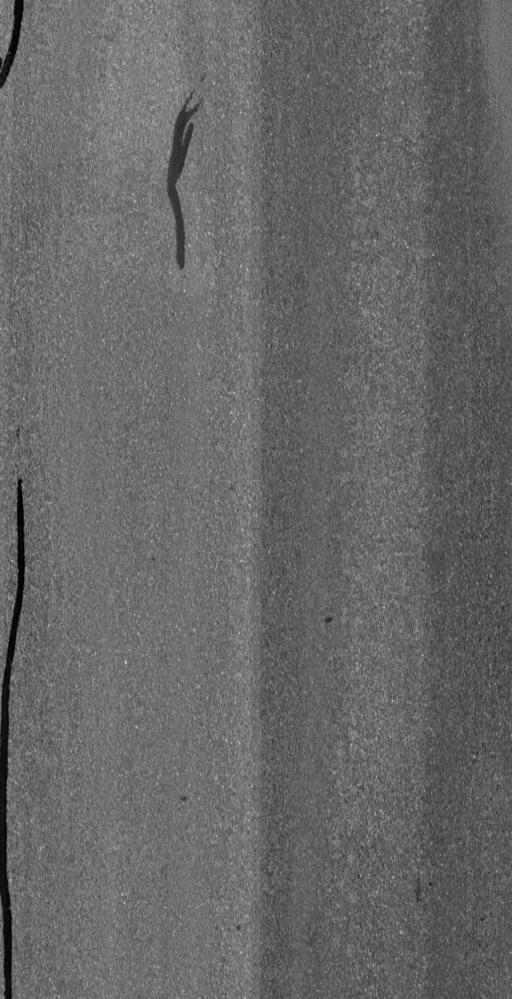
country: US
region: Vermont
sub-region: Chittenden County
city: Burlington
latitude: 44.5247
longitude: -73.2667
